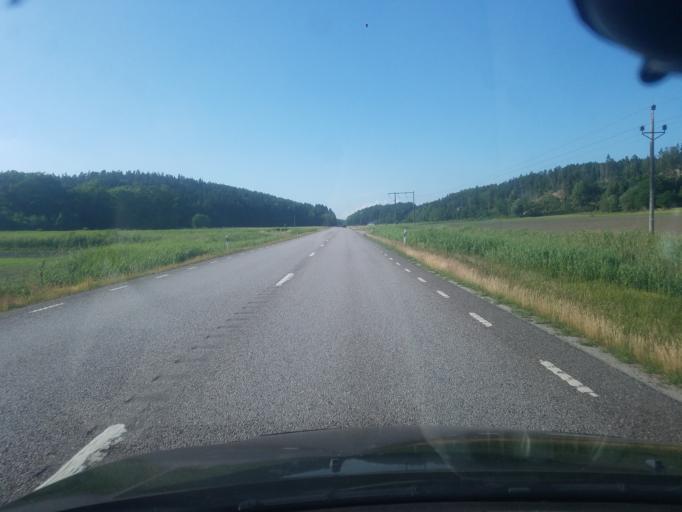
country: SE
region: Vaestra Goetaland
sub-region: Orust
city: Henan
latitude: 58.1733
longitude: 11.6988
